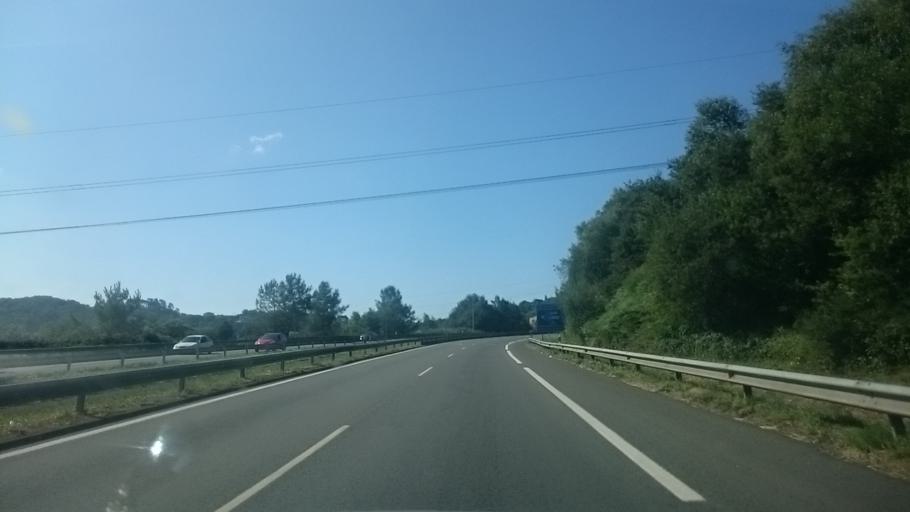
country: ES
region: Asturias
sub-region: Province of Asturias
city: Castandiello
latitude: 43.3179
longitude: -5.8687
